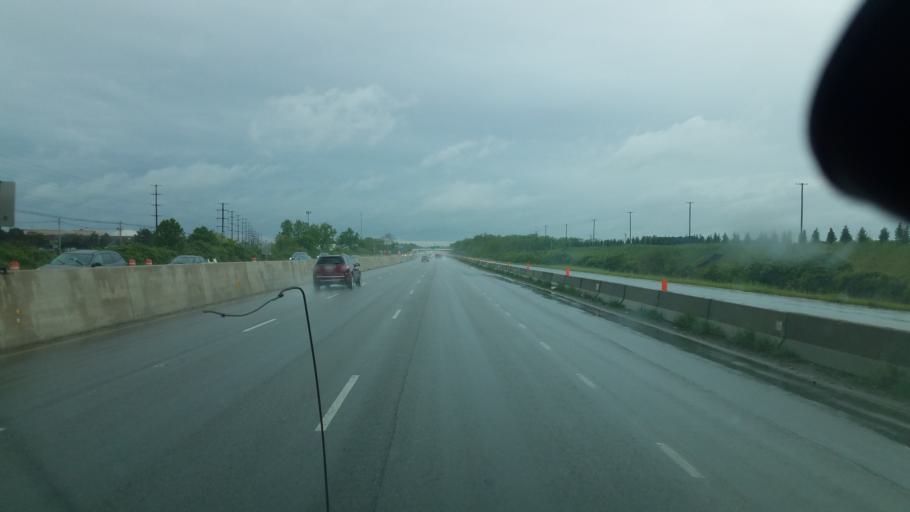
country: US
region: Ohio
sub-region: Franklin County
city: Columbus
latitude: 39.9114
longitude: -83.0216
